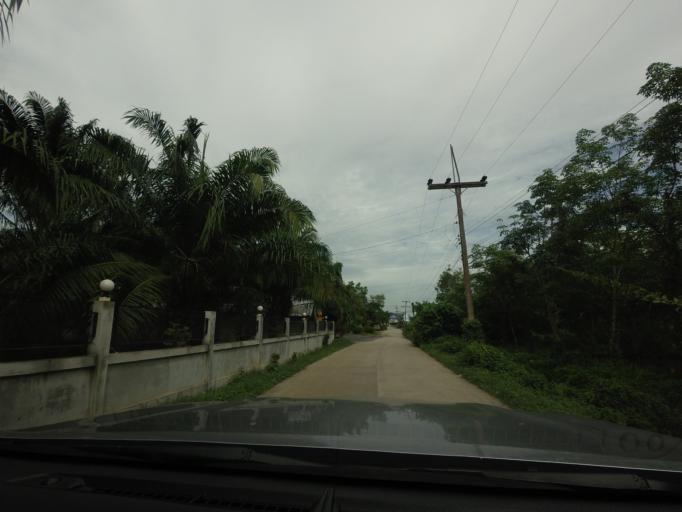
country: TH
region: Nakhon Si Thammarat
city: Phra Phrom
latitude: 8.2829
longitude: 99.9090
